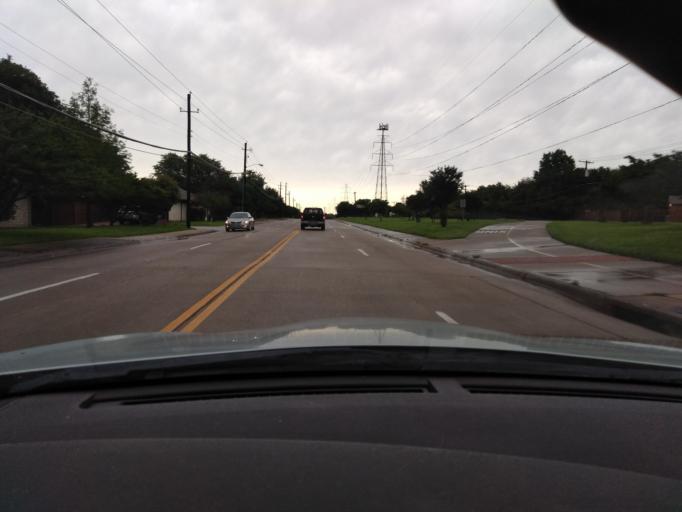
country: US
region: Texas
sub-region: Dallas County
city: Addison
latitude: 32.9662
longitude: -96.7785
